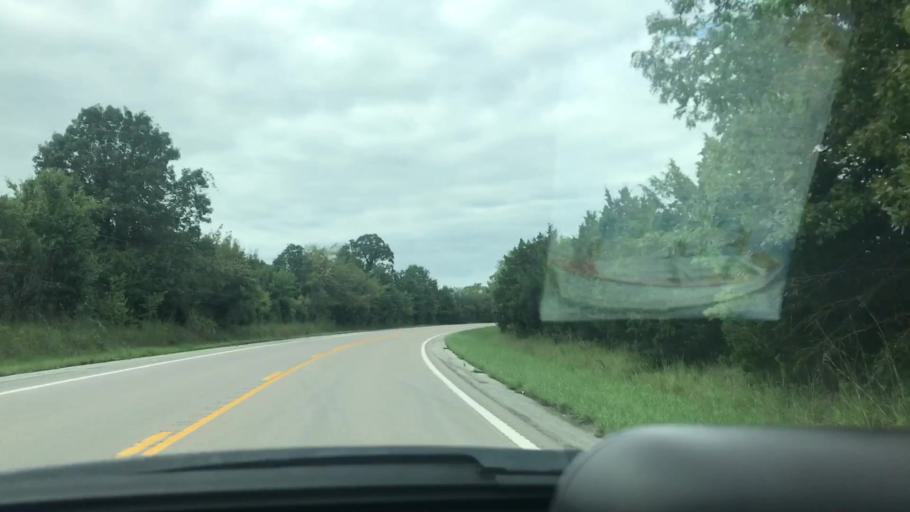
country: US
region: Missouri
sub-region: Benton County
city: Warsaw
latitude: 38.1249
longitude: -93.2799
